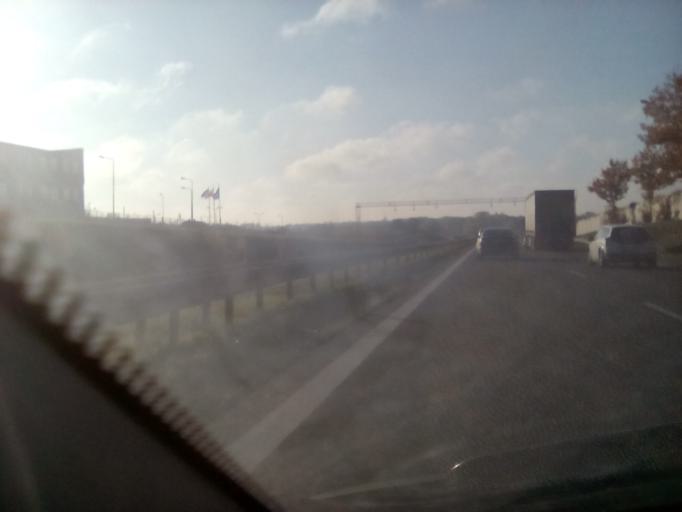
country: PL
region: Masovian Voivodeship
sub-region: Powiat grojecki
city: Grojec
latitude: 51.8855
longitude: 20.8560
